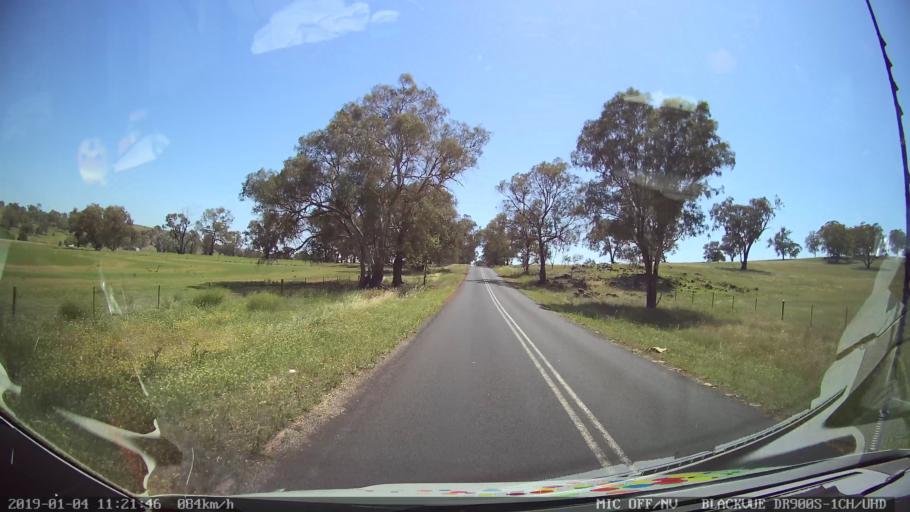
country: AU
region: New South Wales
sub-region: Cabonne
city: Molong
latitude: -33.1520
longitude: 148.7148
